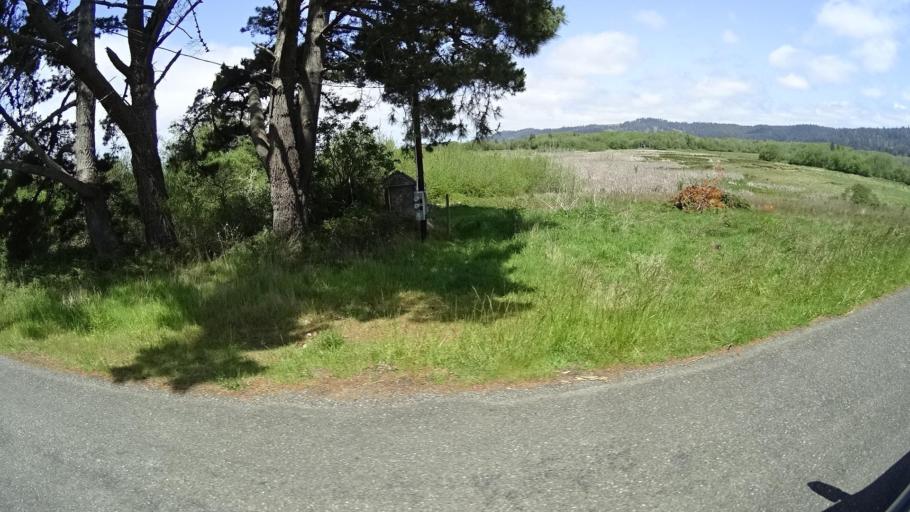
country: US
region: California
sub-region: Humboldt County
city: Humboldt Hill
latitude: 40.6718
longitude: -124.2137
